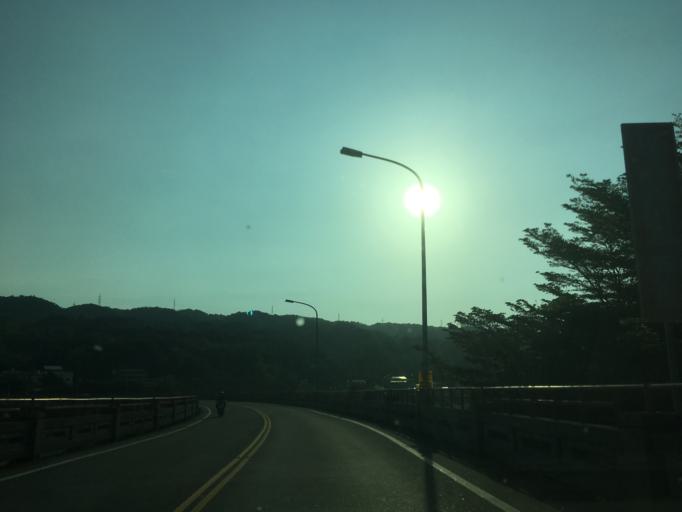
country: TW
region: Taiwan
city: Zhongxing New Village
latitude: 23.9529
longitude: 120.6594
